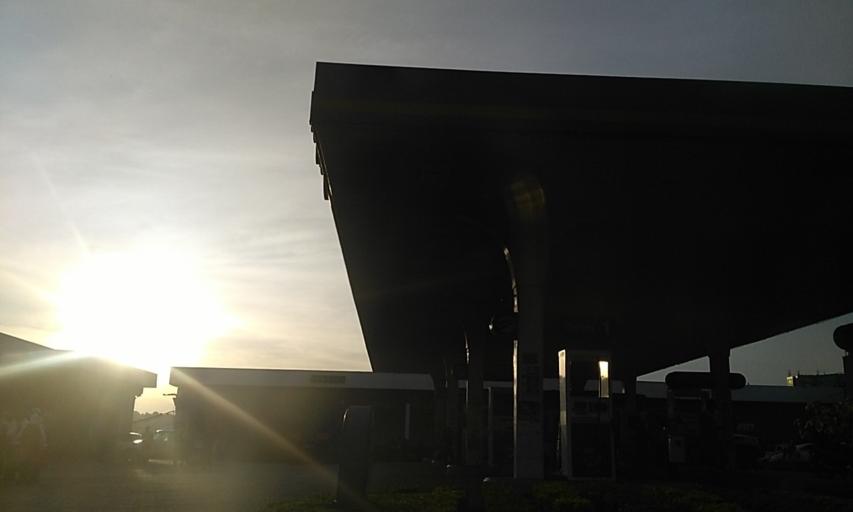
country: UG
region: Central Region
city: Kampala Central Division
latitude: 0.3255
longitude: 32.5741
